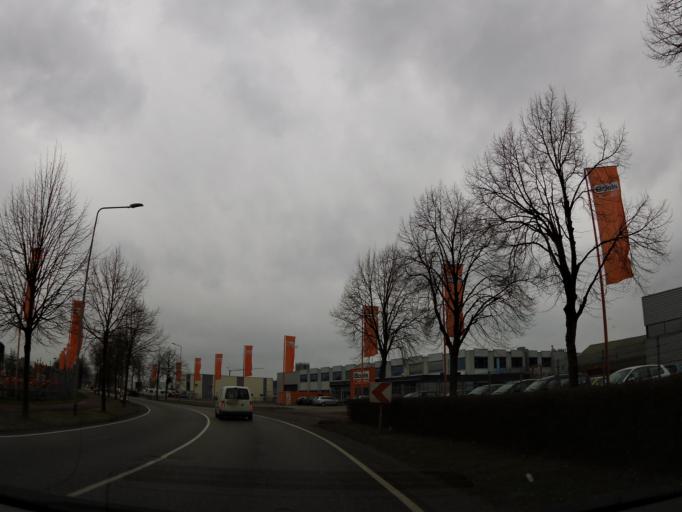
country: NL
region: Limburg
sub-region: Gemeente Sittard-Geleen
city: Sittard
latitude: 51.0192
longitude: 5.8706
